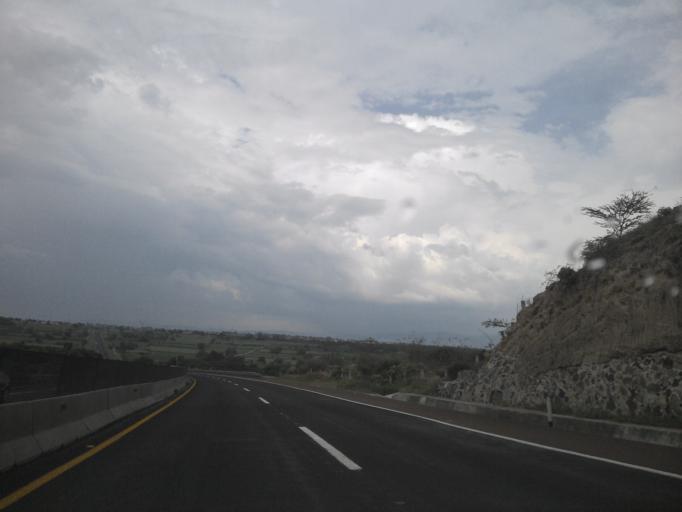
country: MX
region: Hidalgo
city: San Marcos
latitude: 20.0747
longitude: -99.3542
